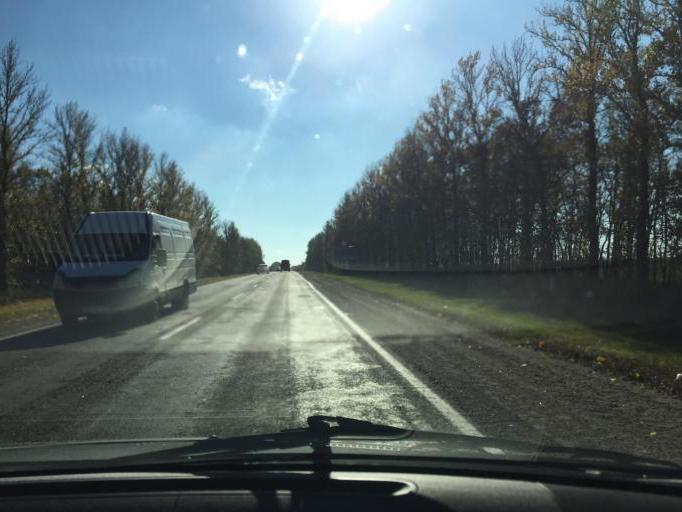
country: BY
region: Minsk
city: Salihorsk
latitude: 52.8988
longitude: 27.4751
